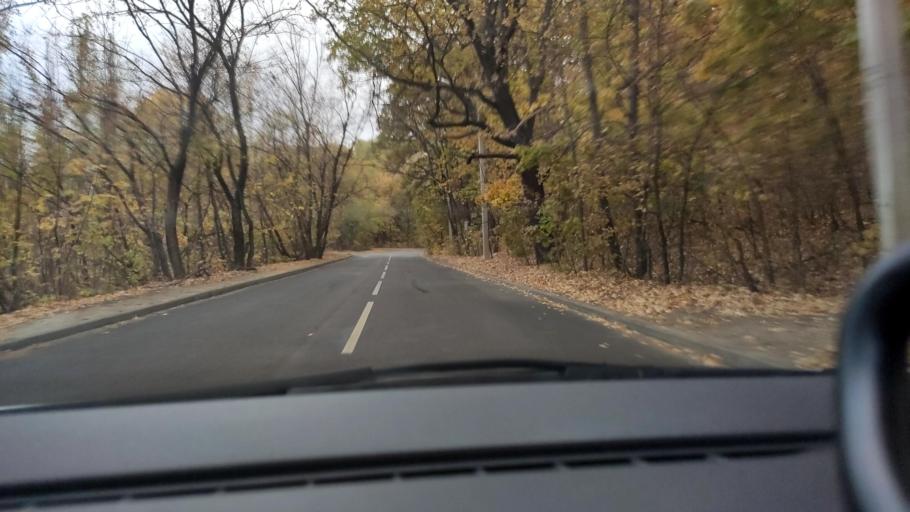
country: RU
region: Voronezj
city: Voronezh
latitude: 51.7234
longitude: 39.2363
